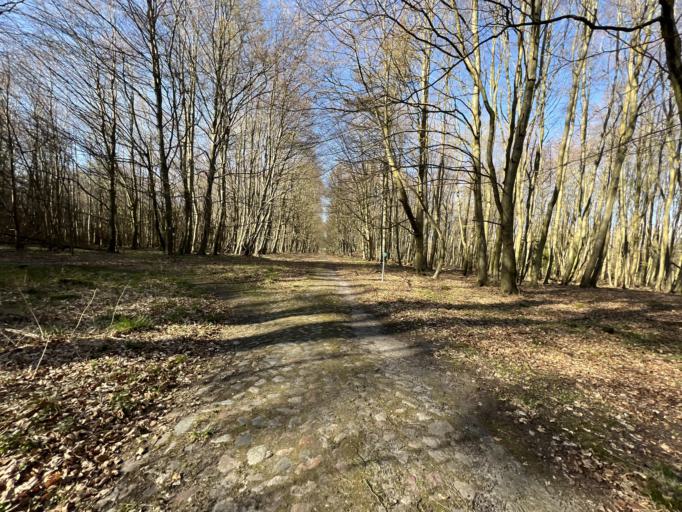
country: DE
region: Mecklenburg-Vorpommern
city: Sassnitz
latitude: 54.5322
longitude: 13.6432
